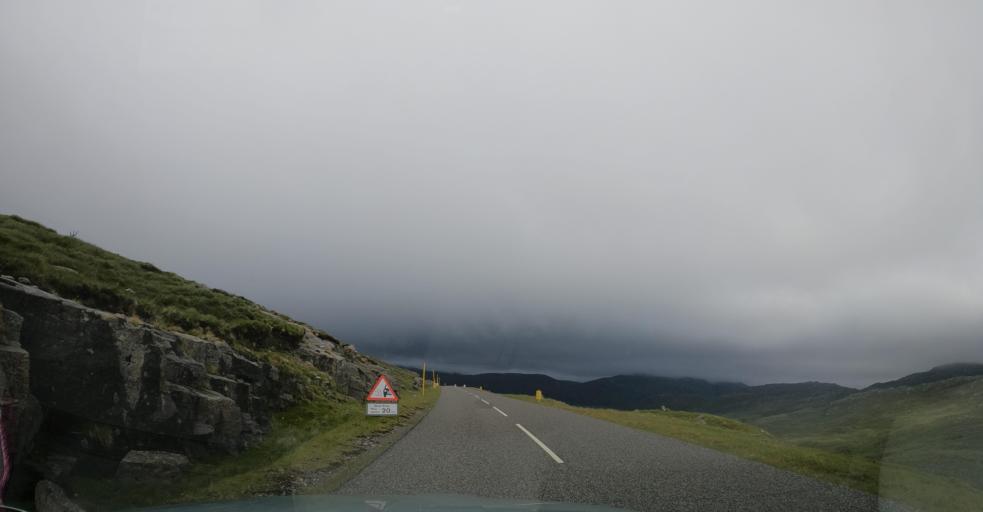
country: GB
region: Scotland
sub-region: Eilean Siar
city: Harris
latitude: 57.9564
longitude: -6.7575
